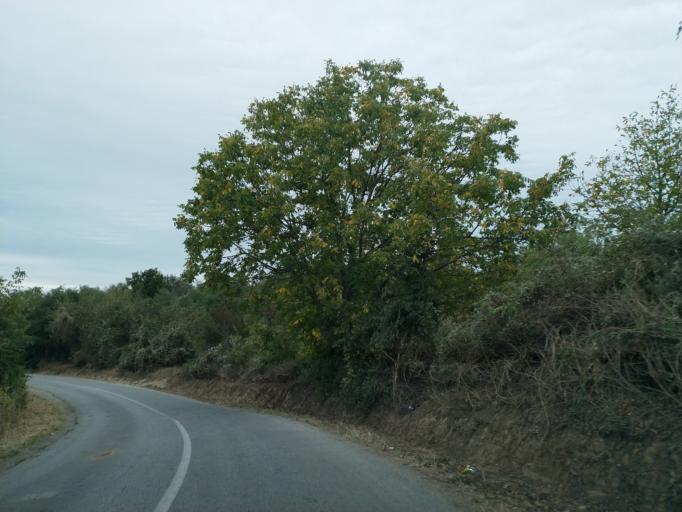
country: RS
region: Central Serbia
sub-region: Pomoravski Okrug
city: Paracin
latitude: 43.8527
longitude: 21.3231
